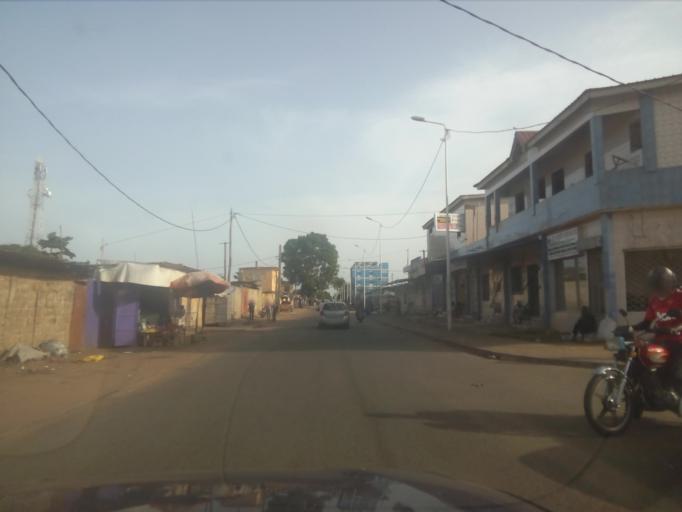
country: TG
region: Maritime
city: Lome
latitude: 6.1446
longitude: 1.2289
